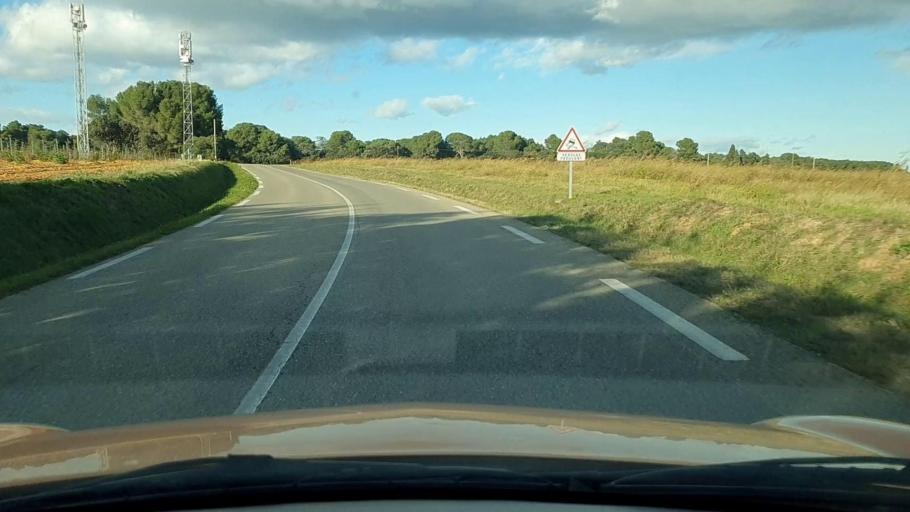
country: FR
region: Languedoc-Roussillon
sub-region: Departement du Gard
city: Vauvert
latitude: 43.6608
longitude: 4.2855
